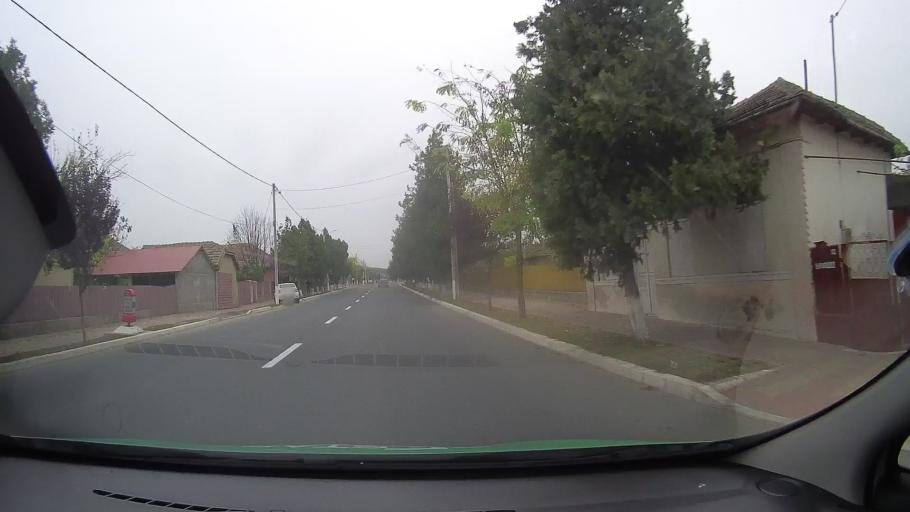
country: RO
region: Constanta
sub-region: Oras Harsova
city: Harsova
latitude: 44.6890
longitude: 27.9467
